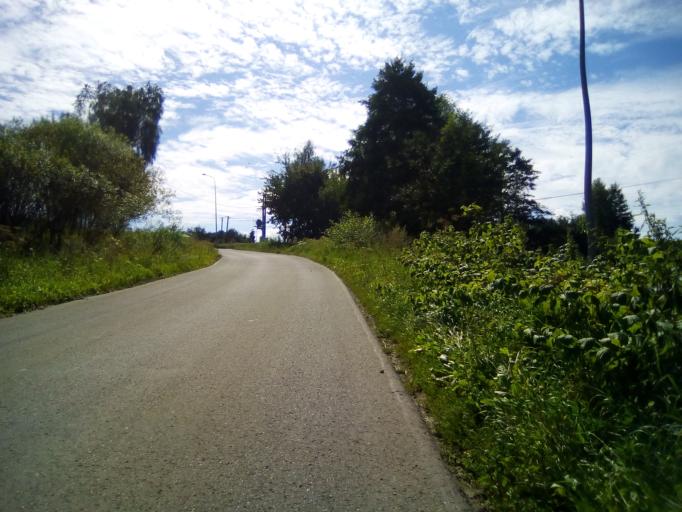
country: PL
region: Subcarpathian Voivodeship
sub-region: Powiat strzyzowski
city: Konieczkowa
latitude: 49.8271
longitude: 21.9271
